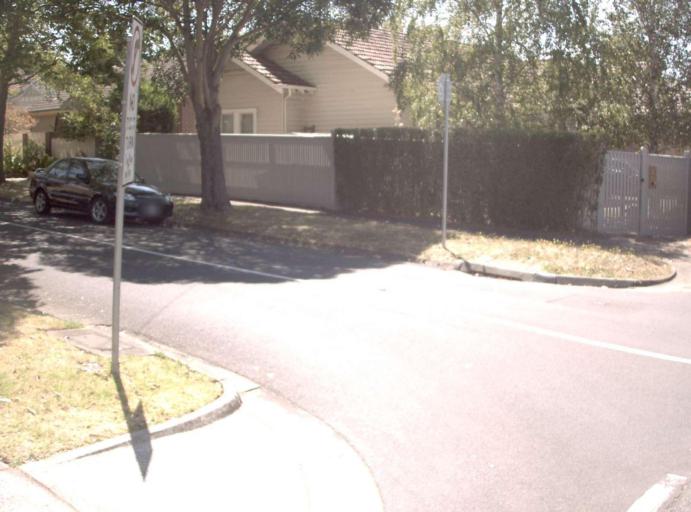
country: AU
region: Victoria
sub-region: Boroondara
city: Canterbury
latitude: -37.8347
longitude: 145.0872
